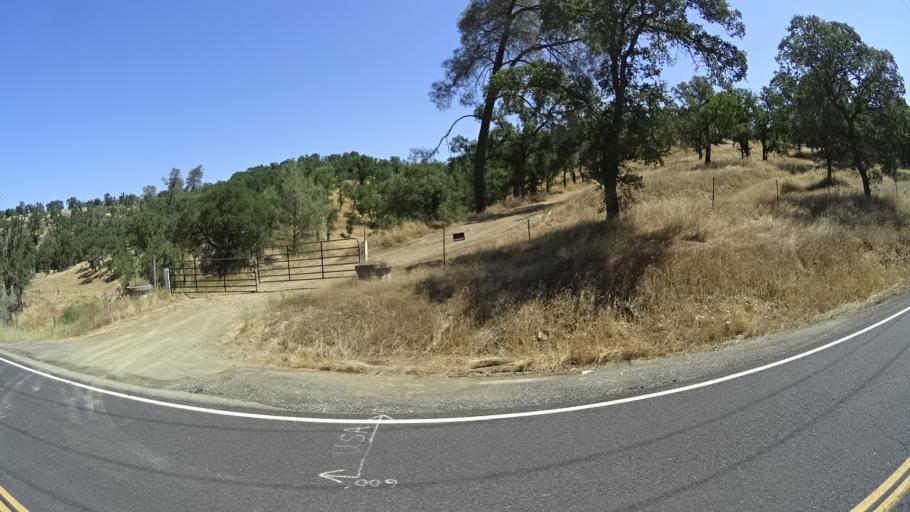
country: US
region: California
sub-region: Calaveras County
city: Copperopolis
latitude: 37.9374
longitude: -120.6337
